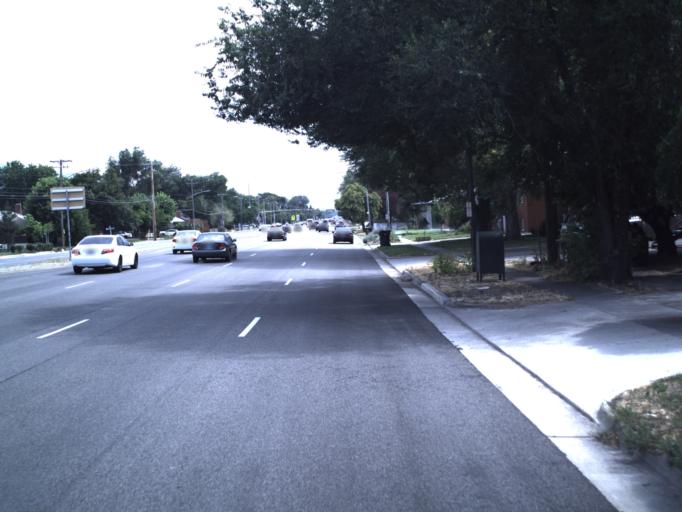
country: US
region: Utah
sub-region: Salt Lake County
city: South Salt Lake
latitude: 40.7163
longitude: -111.8714
